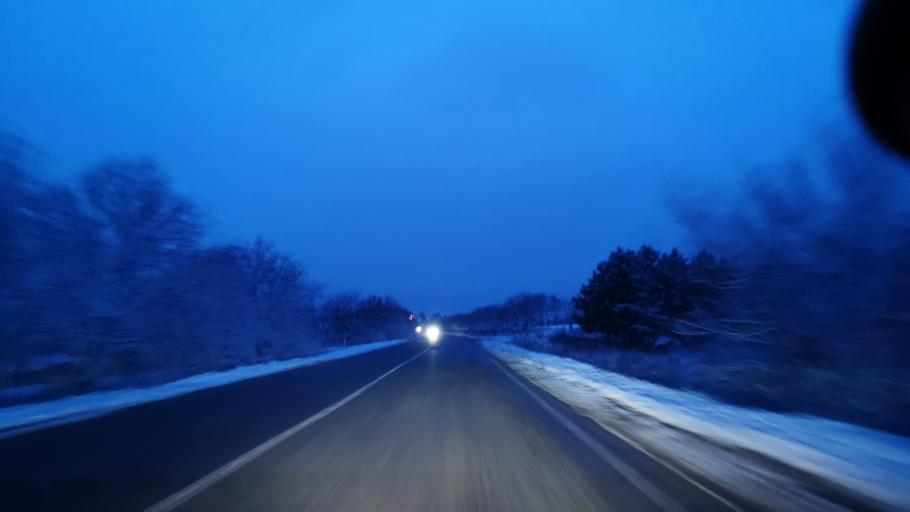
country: MD
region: Orhei
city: Orhei
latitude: 47.5482
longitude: 28.7927
